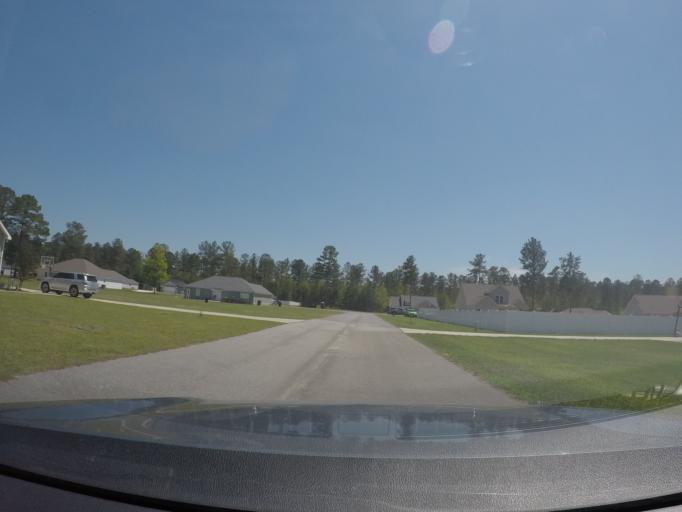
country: US
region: Georgia
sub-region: Bulloch County
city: Brooklet
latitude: 32.3491
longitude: -81.7561
